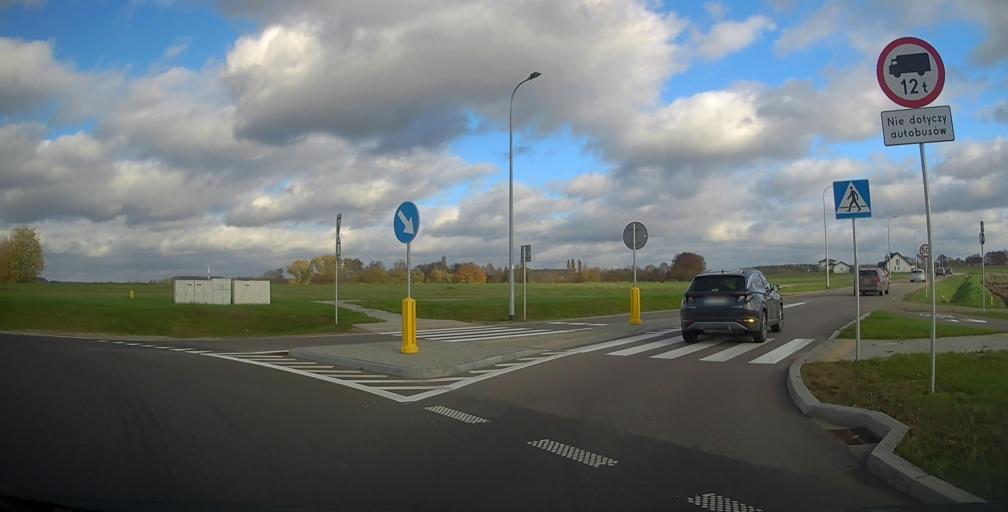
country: PL
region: Podlasie
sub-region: Powiat lomzynski
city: Piatnica
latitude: 53.2489
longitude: 22.1082
